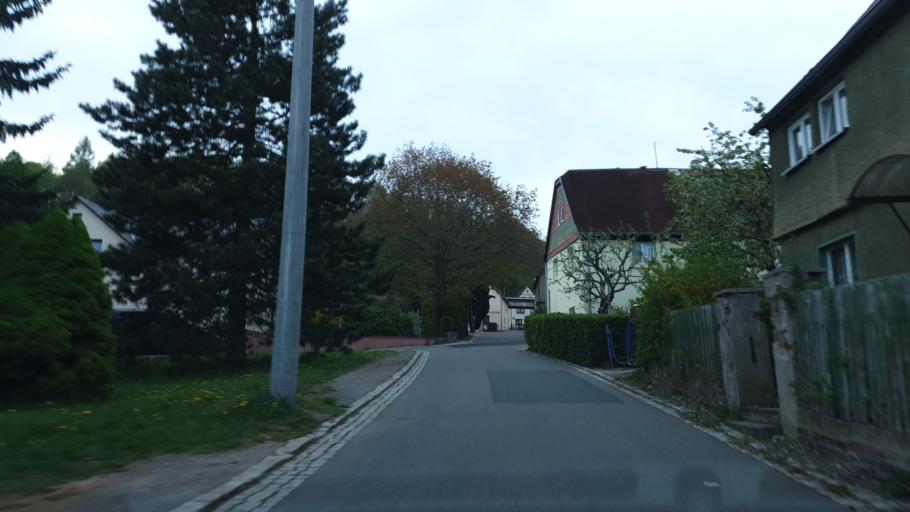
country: DE
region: Saxony
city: Oelsnitz
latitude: 50.7239
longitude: 12.6982
